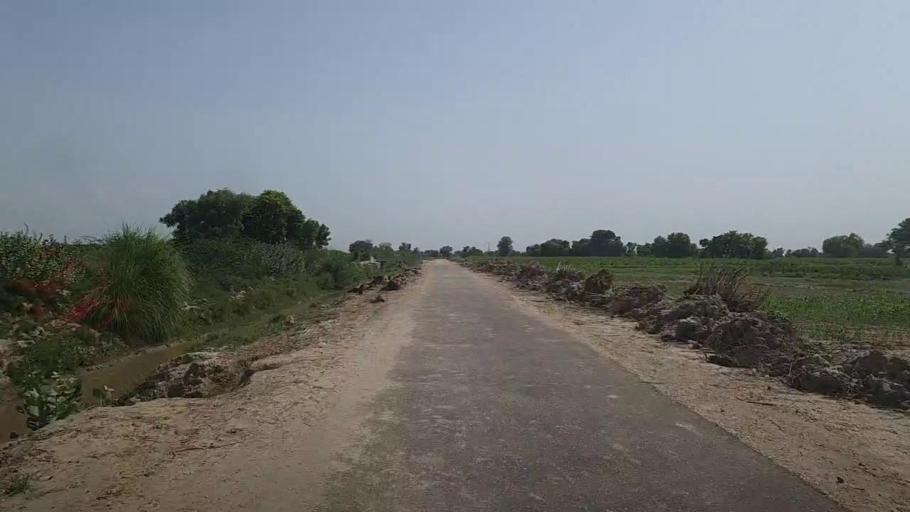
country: PK
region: Sindh
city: Pad Idan
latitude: 26.8284
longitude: 68.3298
